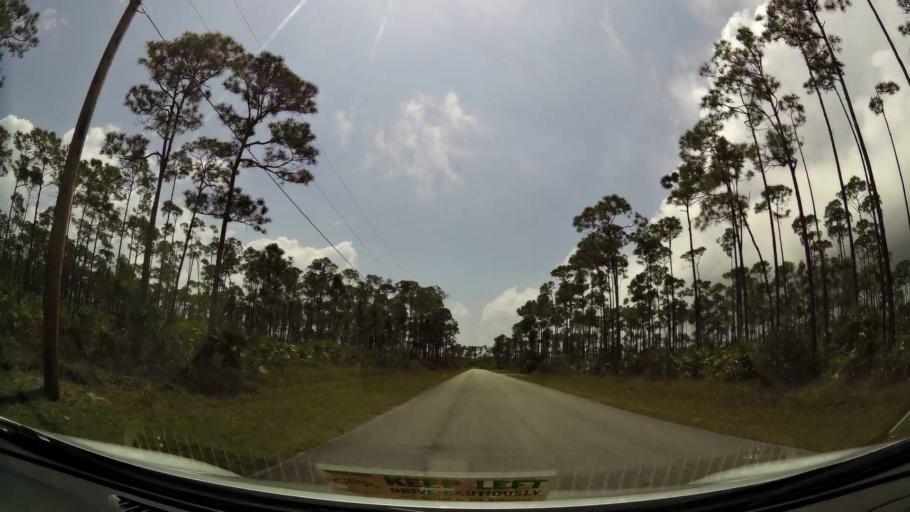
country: BS
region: Freeport
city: Lucaya
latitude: 26.5315
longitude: -78.6350
